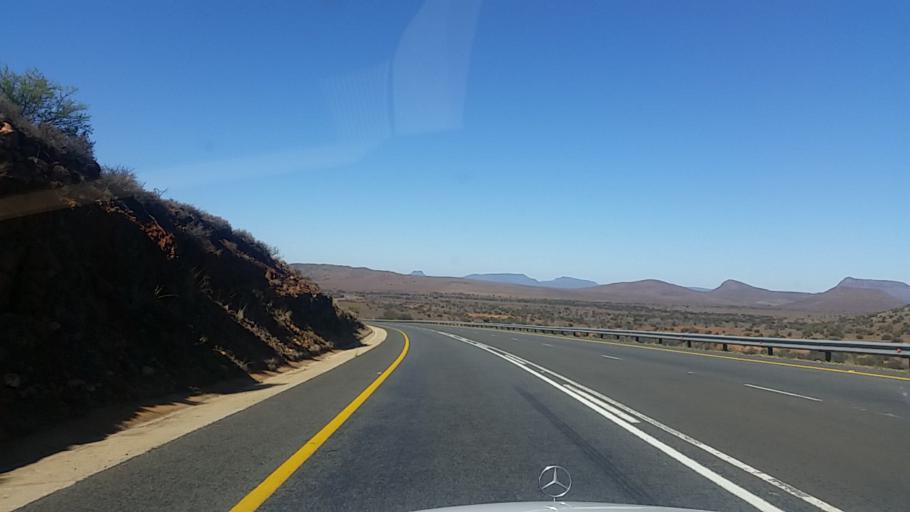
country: ZA
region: Eastern Cape
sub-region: Cacadu District Municipality
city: Graaff-Reinet
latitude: -32.0614
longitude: 24.6072
